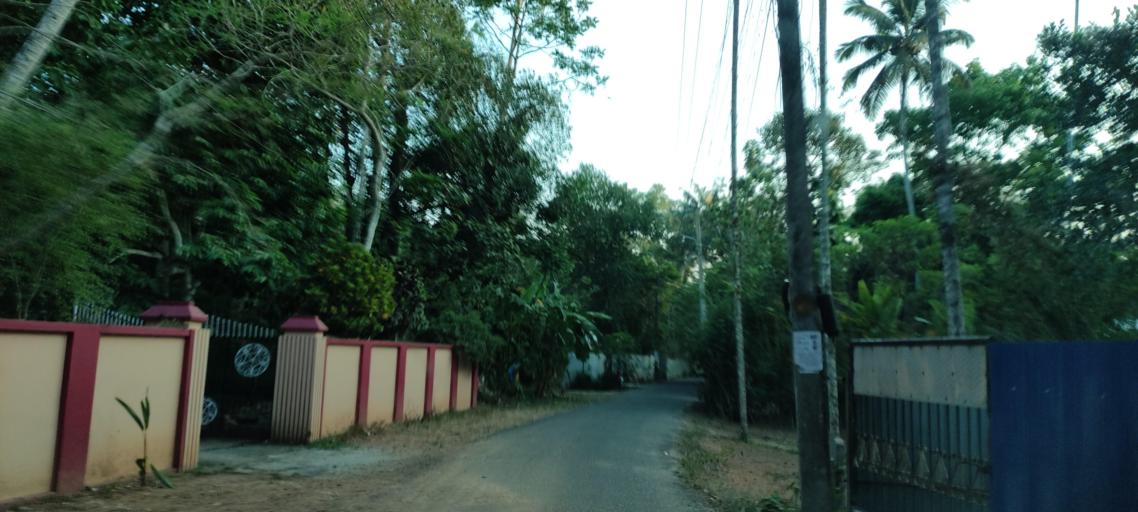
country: IN
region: Kerala
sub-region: Alappuzha
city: Alleppey
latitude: 9.5360
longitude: 76.3342
